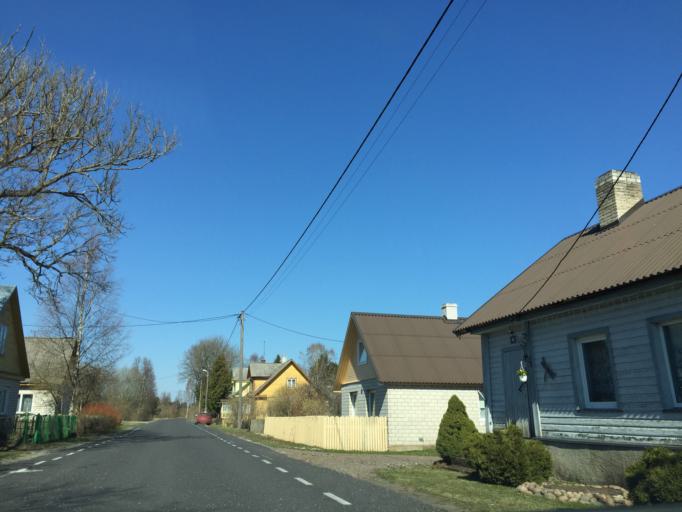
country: EE
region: Jogevamaa
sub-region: Mustvee linn
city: Mustvee
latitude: 58.8597
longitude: 26.9512
